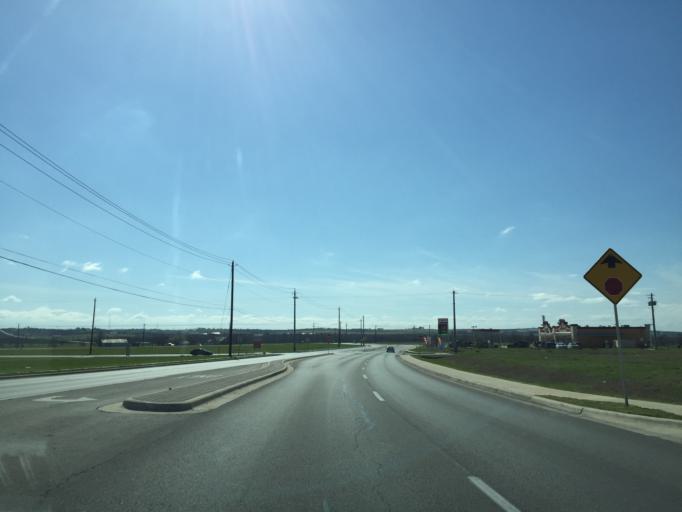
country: US
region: Texas
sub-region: Travis County
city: Garfield
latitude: 30.1573
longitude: -97.6417
